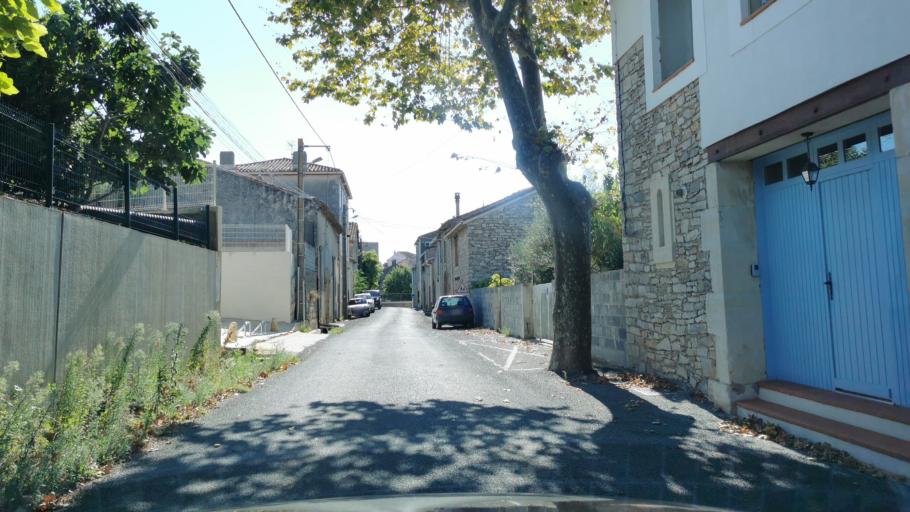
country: FR
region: Languedoc-Roussillon
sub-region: Departement de l'Aude
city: Ginestas
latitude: 43.2494
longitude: 2.8579
